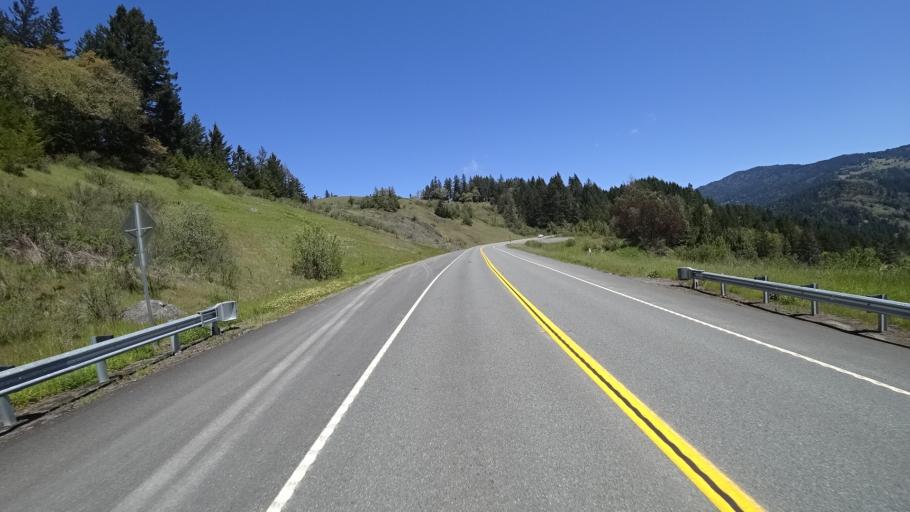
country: US
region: California
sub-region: Humboldt County
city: Blue Lake
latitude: 40.9069
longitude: -123.8286
